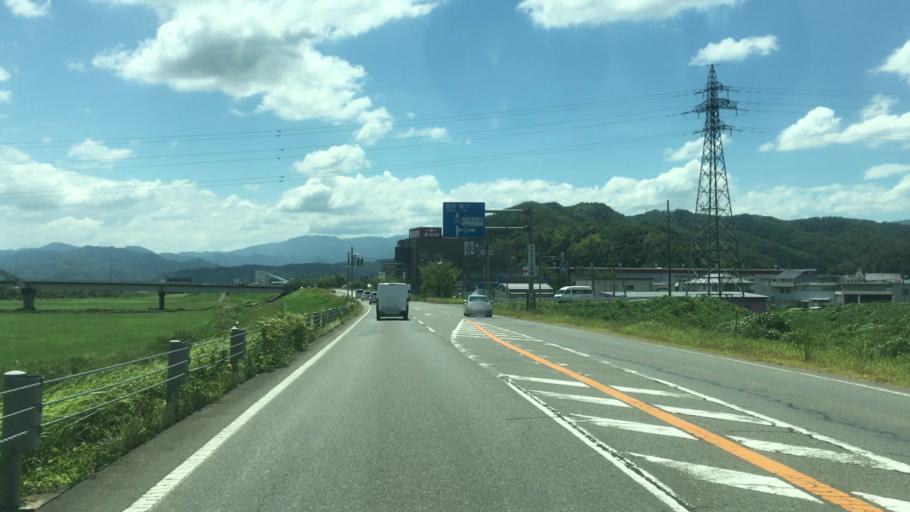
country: JP
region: Hyogo
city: Toyooka
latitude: 35.5088
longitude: 134.8183
